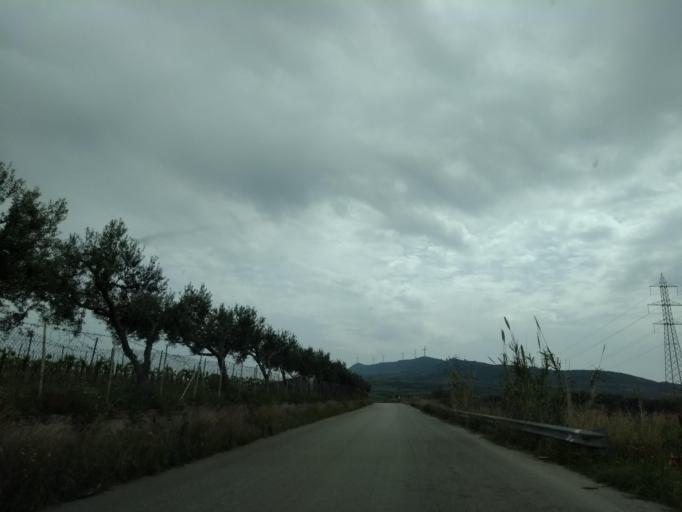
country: IT
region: Sicily
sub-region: Palermo
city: Partinico
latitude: 37.9936
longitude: 13.0659
